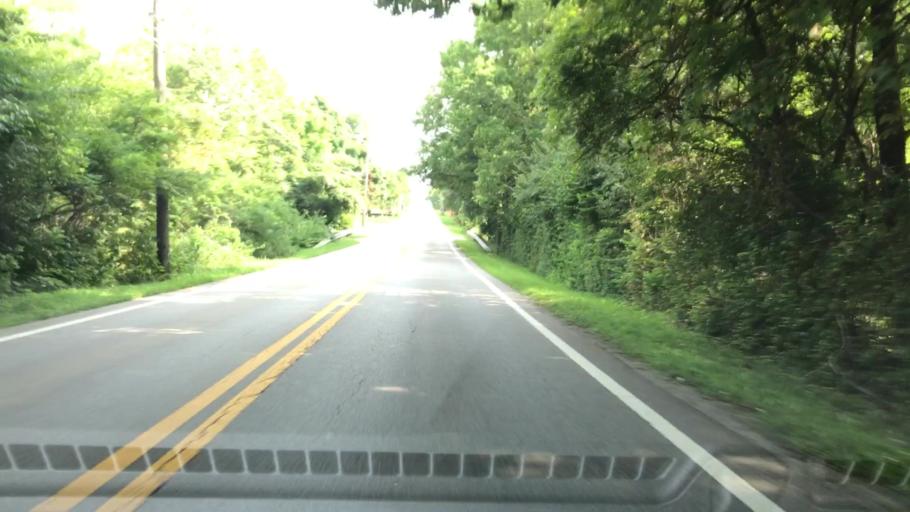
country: US
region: Ohio
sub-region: Franklin County
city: Upper Arlington
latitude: 39.9823
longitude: -83.0870
